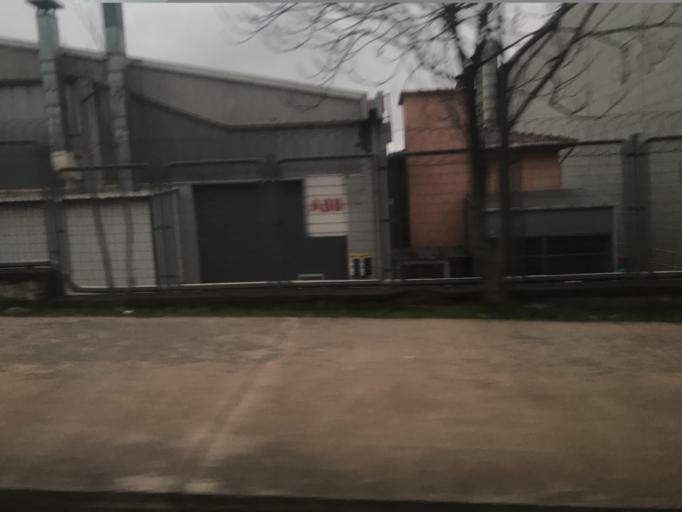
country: TR
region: Istanbul
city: Maltepe
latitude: 40.9095
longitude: 29.2013
